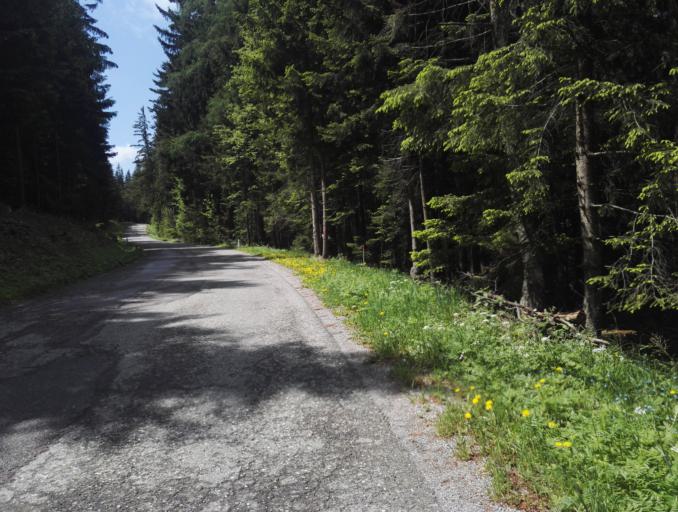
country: AT
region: Styria
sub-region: Politischer Bezirk Weiz
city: Stenzengreith
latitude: 47.2081
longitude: 15.4880
